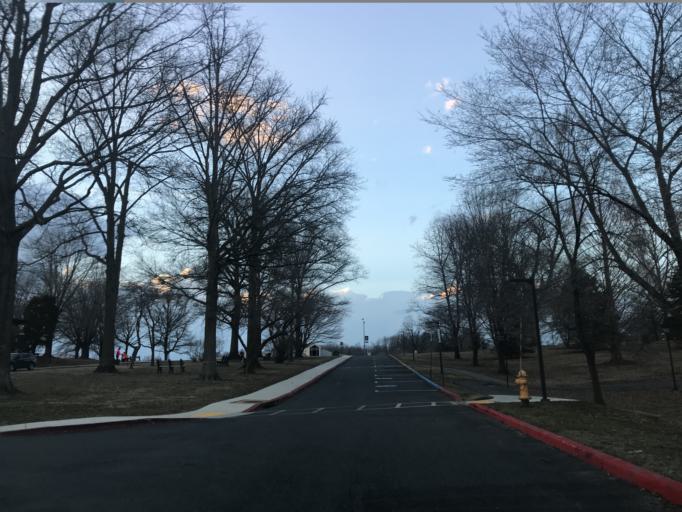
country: US
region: Maryland
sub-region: Harford County
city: South Bel Air
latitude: 39.5594
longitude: -76.2837
